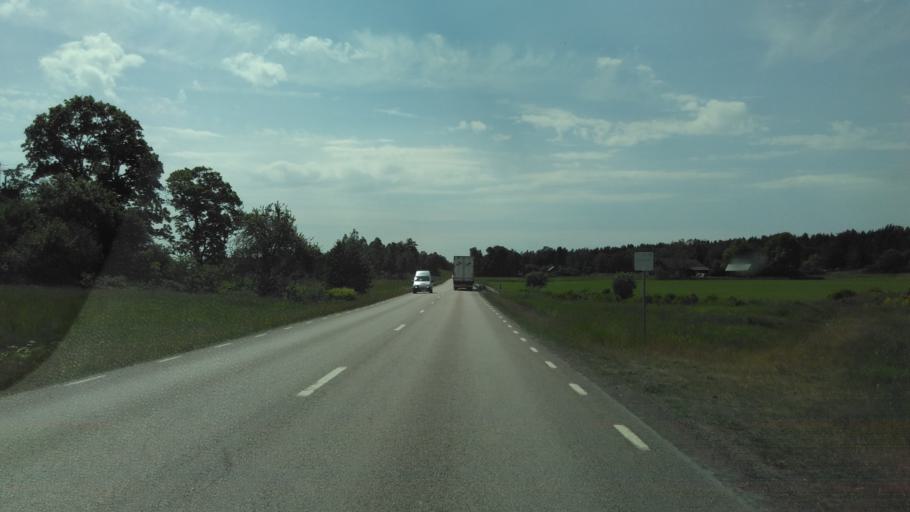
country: SE
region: Vaestra Goetaland
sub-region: Vara Kommun
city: Vara
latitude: 58.4251
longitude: 12.8806
